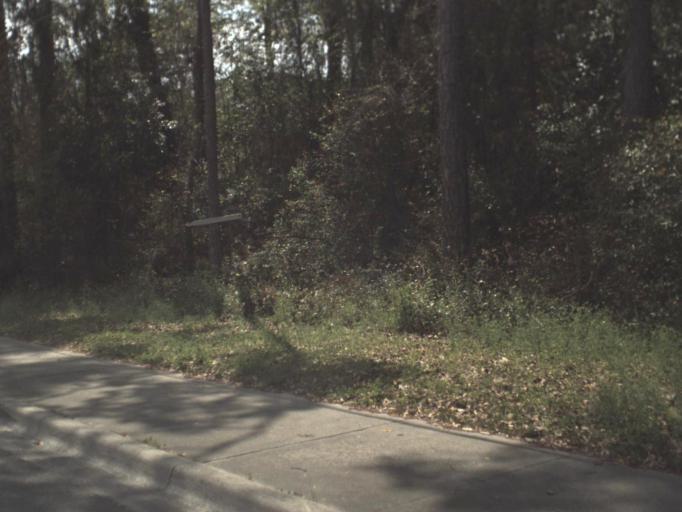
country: US
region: Florida
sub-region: Leon County
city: Tallahassee
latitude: 30.4947
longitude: -84.2454
